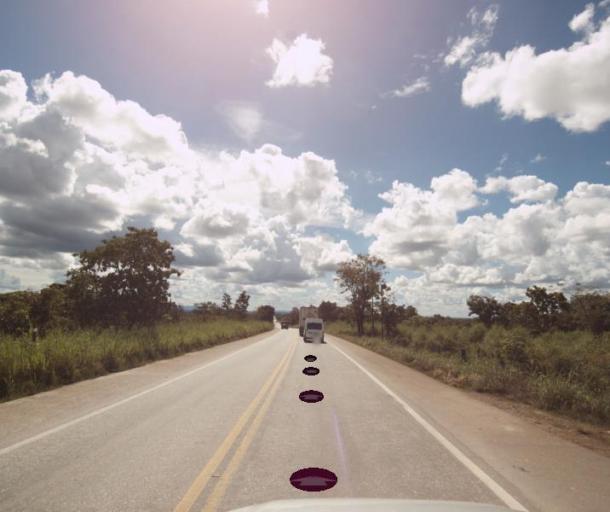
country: BR
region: Goias
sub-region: Porangatu
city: Porangatu
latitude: -13.5735
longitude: -49.0446
